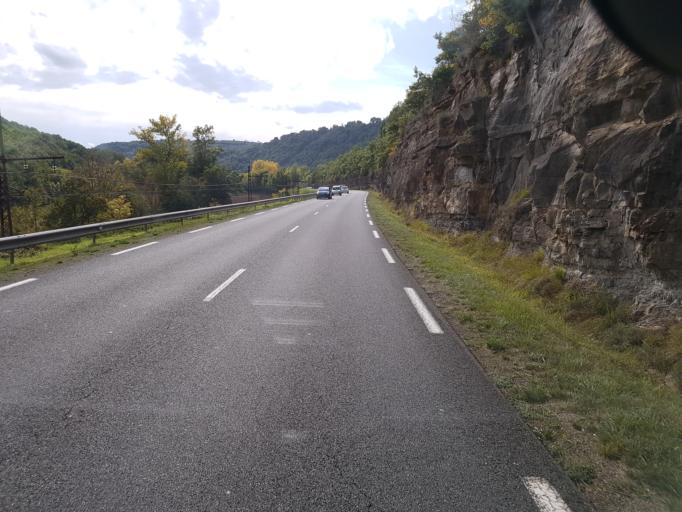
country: FR
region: Midi-Pyrenees
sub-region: Departement de l'Aveyron
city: Saint-Georges-de-Luzencon
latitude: 44.0407
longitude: 2.9669
